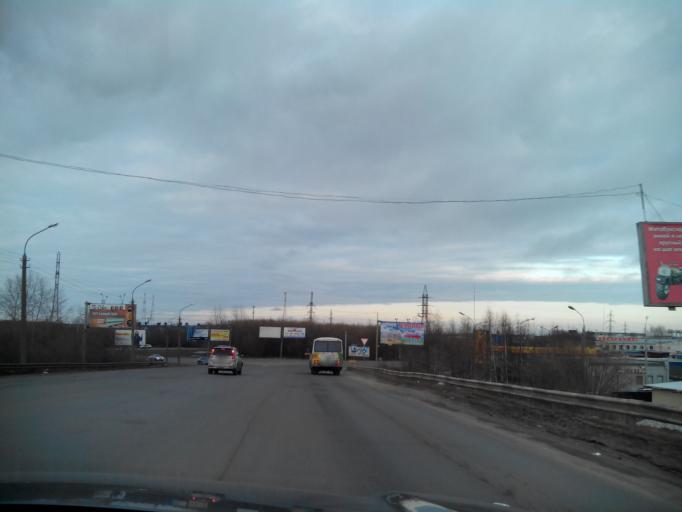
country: RU
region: Arkhangelskaya
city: Arkhangel'sk
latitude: 64.5663
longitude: 40.5638
